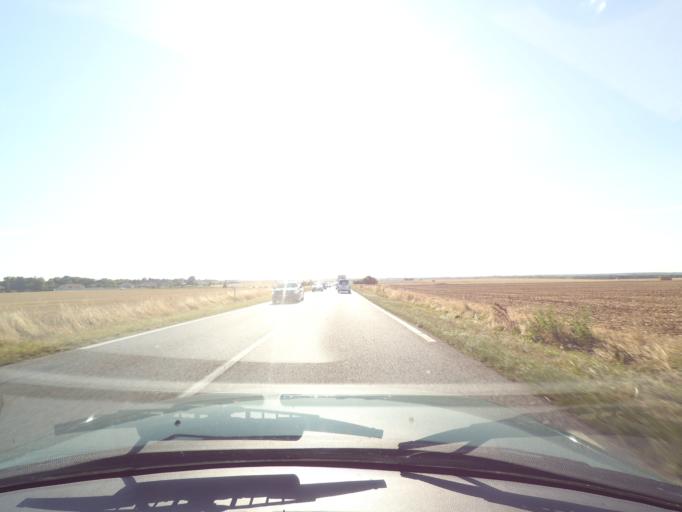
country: FR
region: Poitou-Charentes
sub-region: Departement de la Vienne
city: Vouille
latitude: 46.6523
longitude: 0.1259
